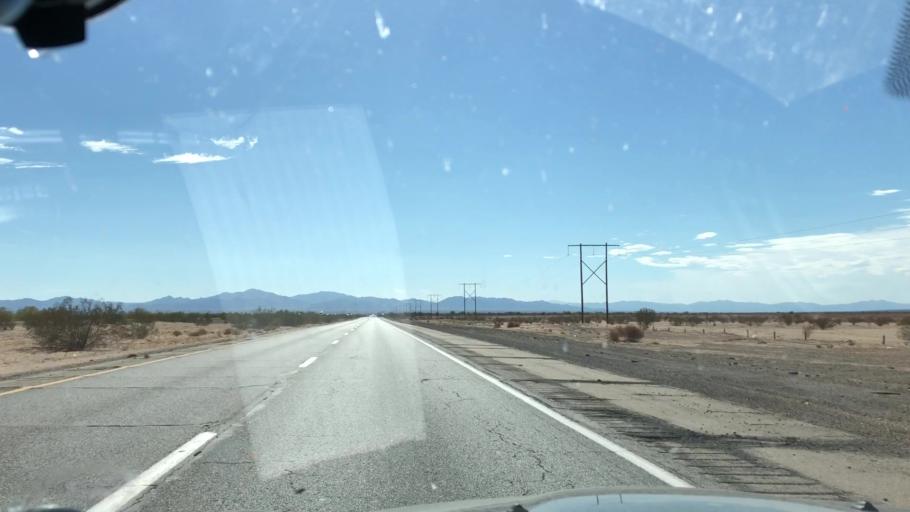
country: US
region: California
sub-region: Riverside County
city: Mesa Verde
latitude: 33.6063
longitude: -114.9569
